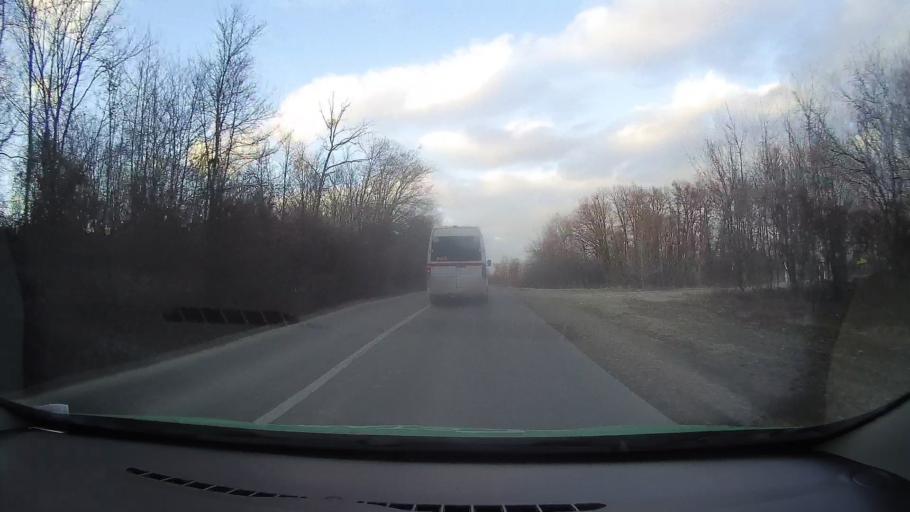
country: RO
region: Dambovita
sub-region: Comuna Gura Ocnitei
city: Gura Ocnitei
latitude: 44.9613
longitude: 25.6006
